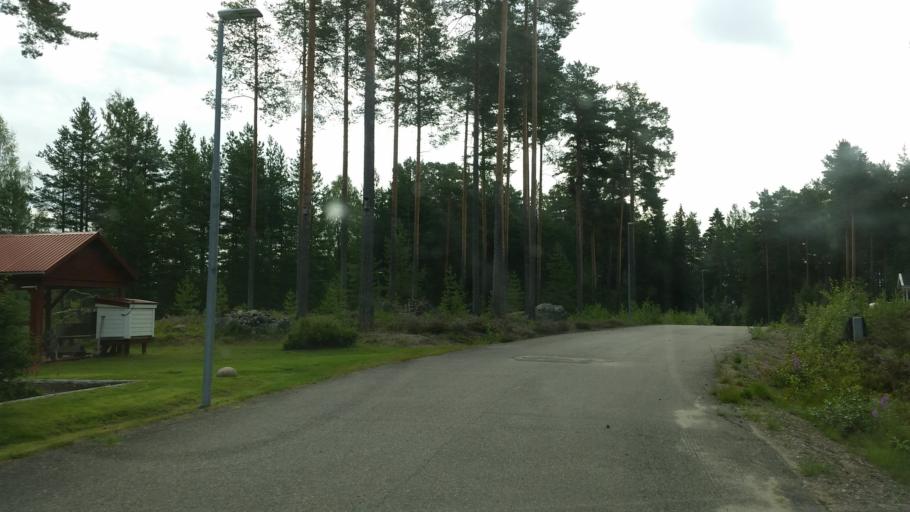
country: SE
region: Vaesternorrland
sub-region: Ange Kommun
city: Ange
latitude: 62.1866
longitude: 15.6433
